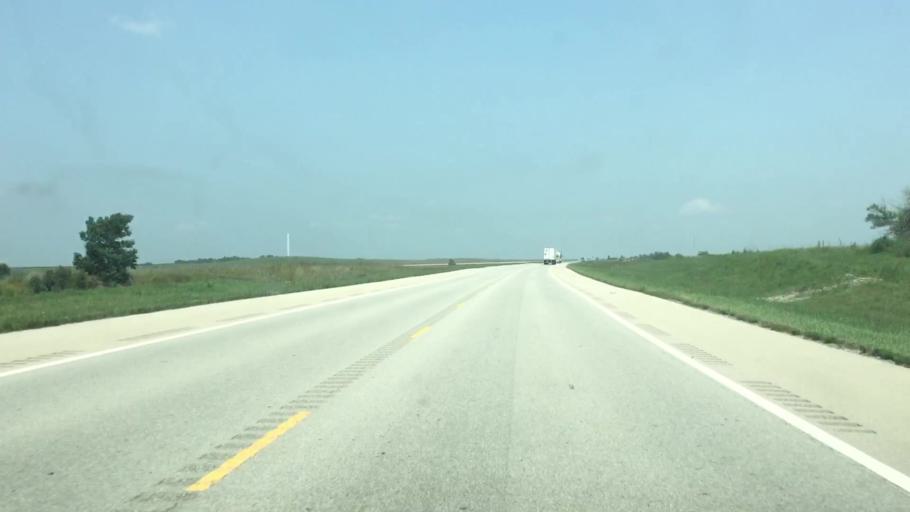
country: US
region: Kansas
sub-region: Allen County
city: Iola
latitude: 38.0746
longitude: -95.3755
